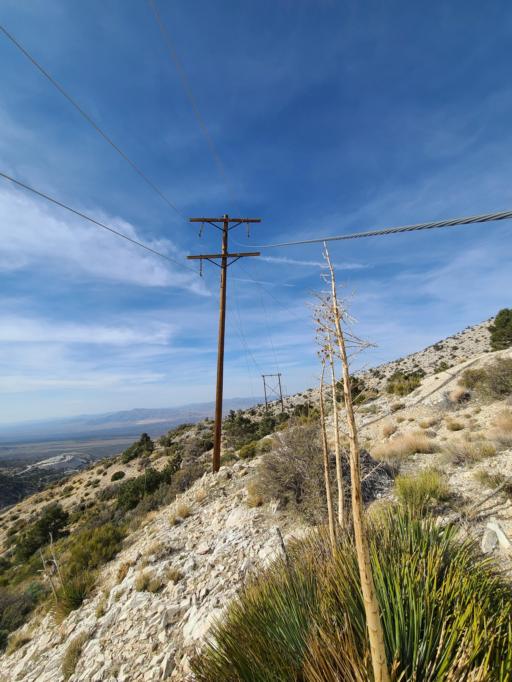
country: US
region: California
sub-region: San Bernardino County
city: Big Bear Lake
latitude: 34.3453
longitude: -116.9130
